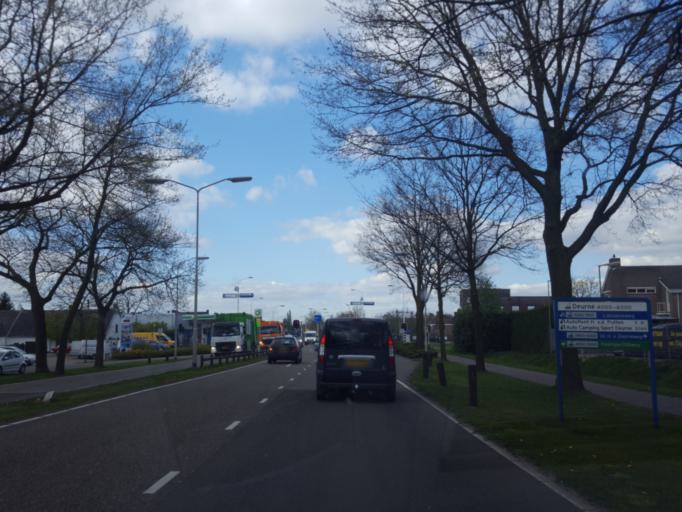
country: NL
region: North Brabant
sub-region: Gemeente Asten
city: Asten
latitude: 51.4528
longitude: 5.7974
